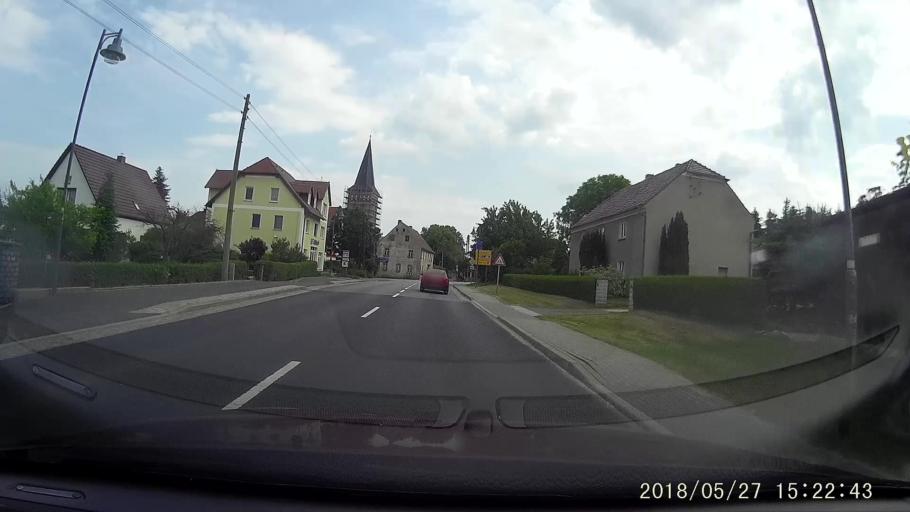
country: DE
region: Saxony
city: Kodersdorf
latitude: 51.2314
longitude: 14.8921
